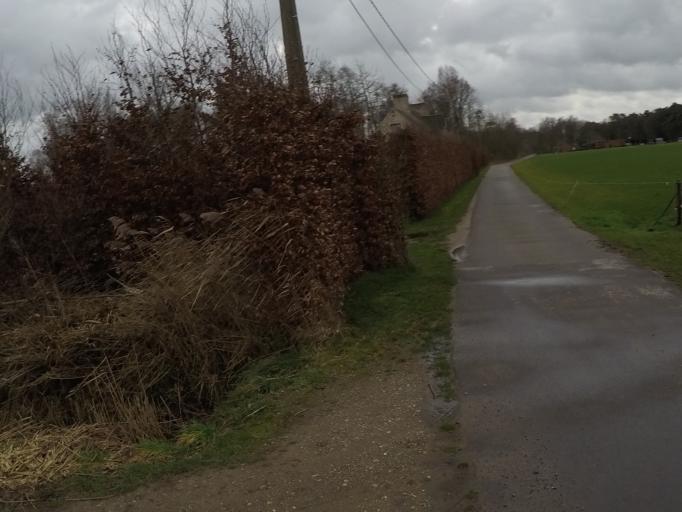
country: BE
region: Flanders
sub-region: Provincie Antwerpen
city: Schilde
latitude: 51.2213
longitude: 4.6186
